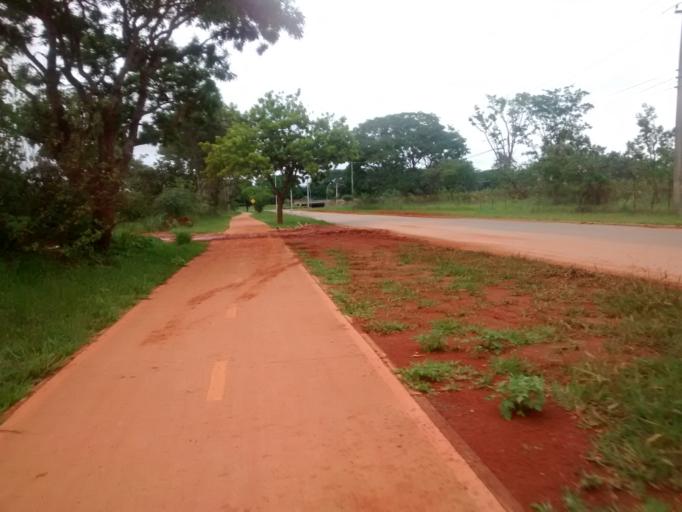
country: BR
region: Federal District
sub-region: Brasilia
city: Brasilia
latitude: -15.8038
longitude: -47.8481
